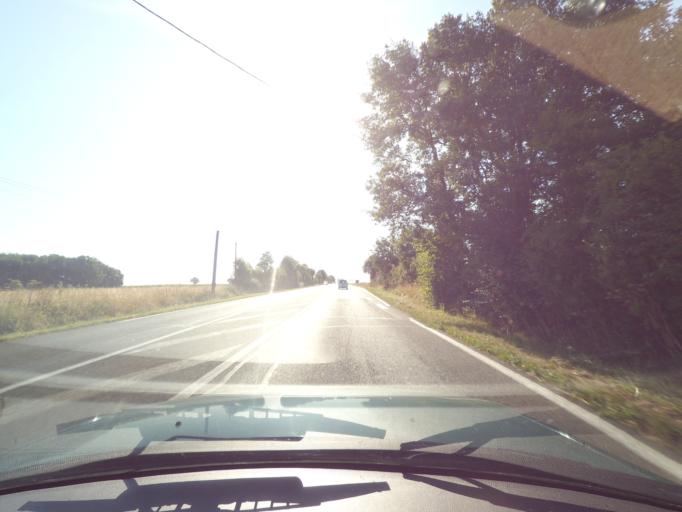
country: FR
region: Poitou-Charentes
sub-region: Departement de la Vienne
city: Ayron
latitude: 46.6584
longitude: 0.0879
